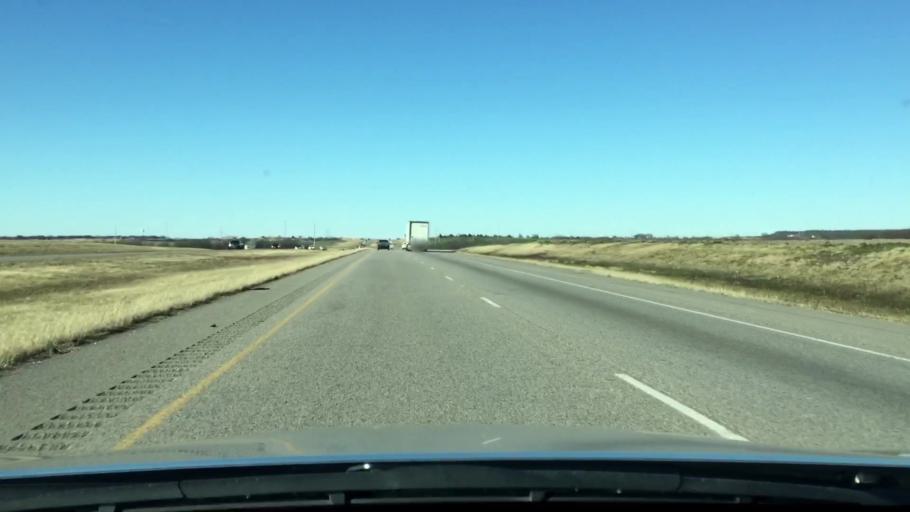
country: US
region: Texas
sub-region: Hill County
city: Itasca
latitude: 32.1282
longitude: -97.1185
